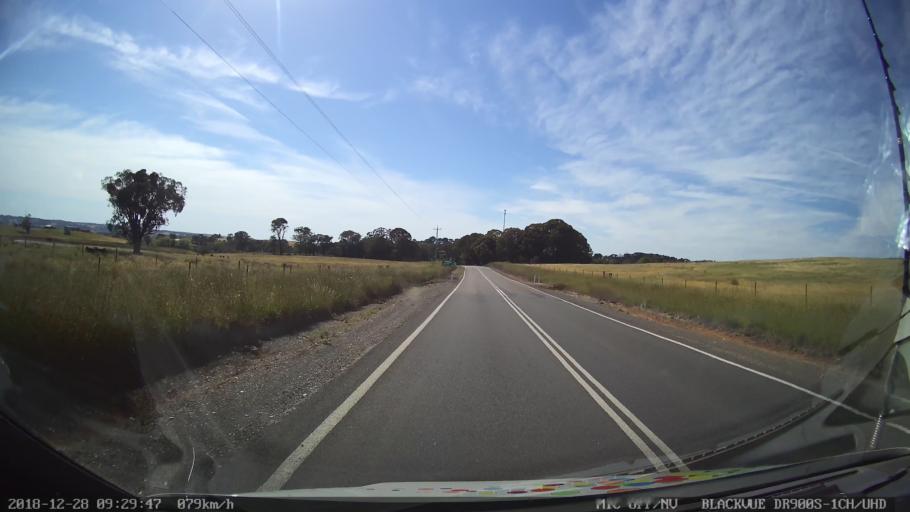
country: AU
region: New South Wales
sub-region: Upper Lachlan Shire
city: Crookwell
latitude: -34.4487
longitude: 149.4319
